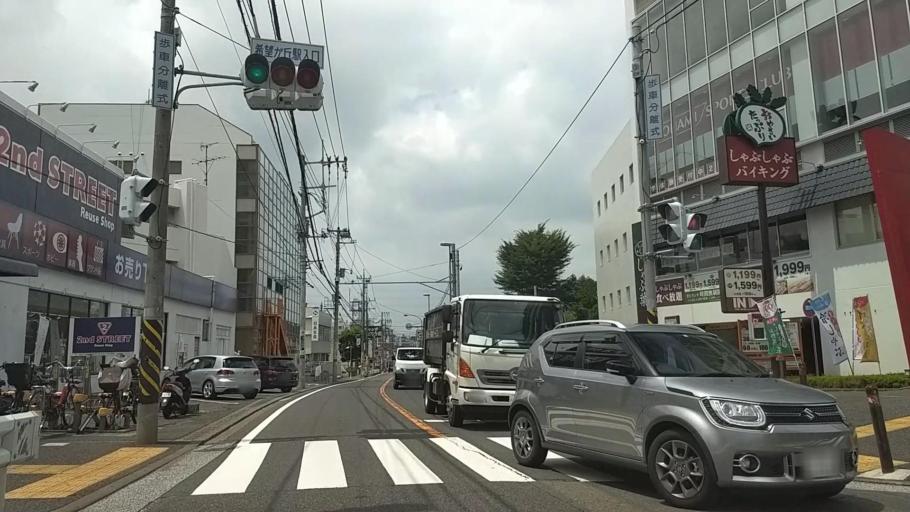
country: JP
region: Kanagawa
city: Minami-rinkan
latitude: 35.4612
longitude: 139.5157
